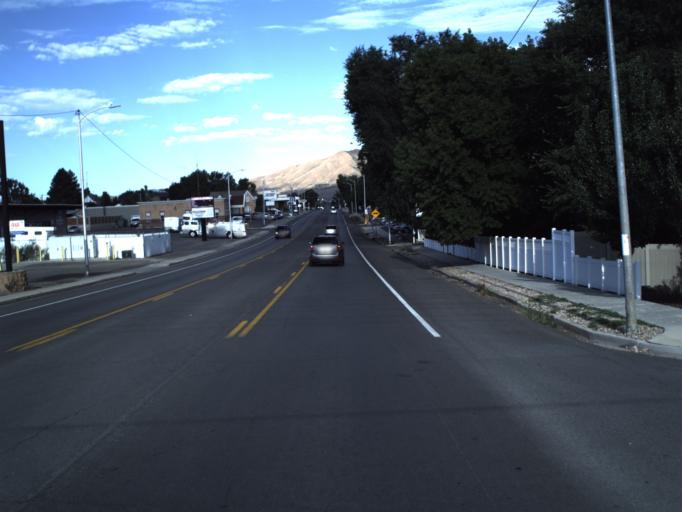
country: US
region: Utah
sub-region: Utah County
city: Payson
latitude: 40.0446
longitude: -111.7254
